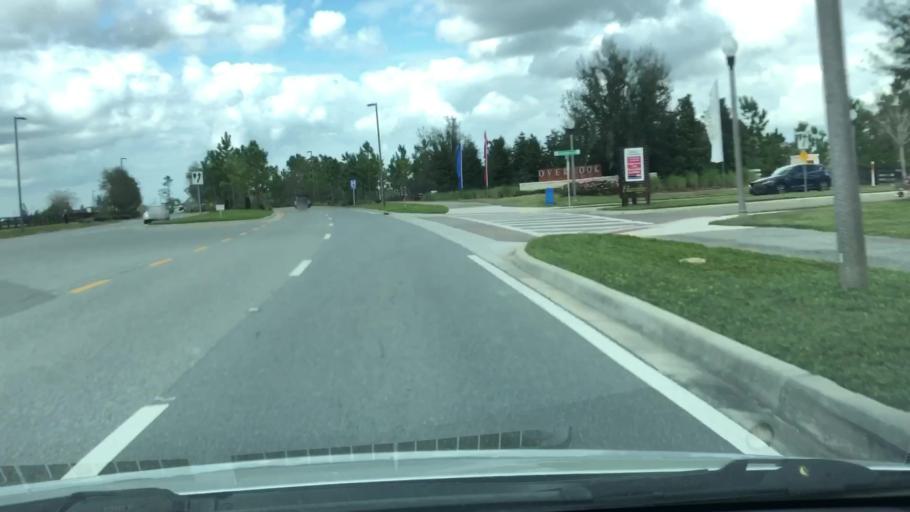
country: US
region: Florida
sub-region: Orange County
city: Lake Butler
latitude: 28.4584
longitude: -81.6239
